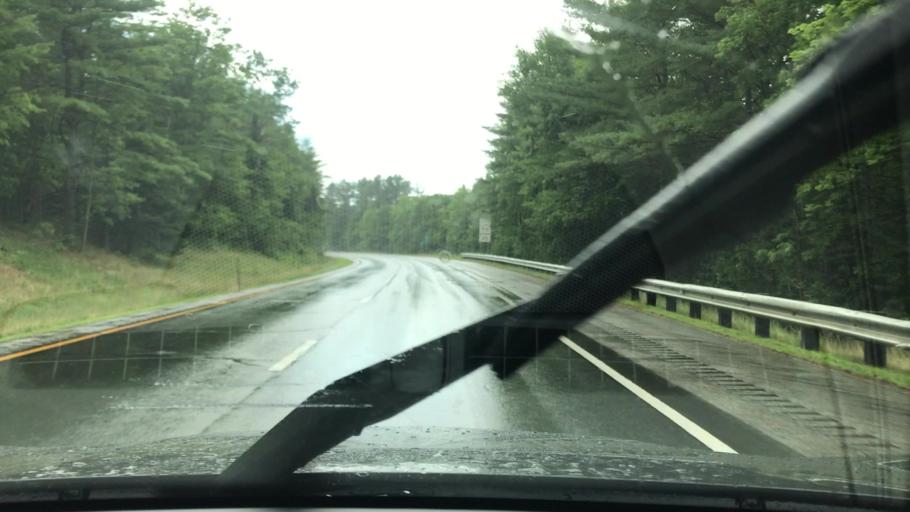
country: US
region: New Hampshire
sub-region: Grafton County
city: Littleton
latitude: 44.3011
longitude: -71.7749
